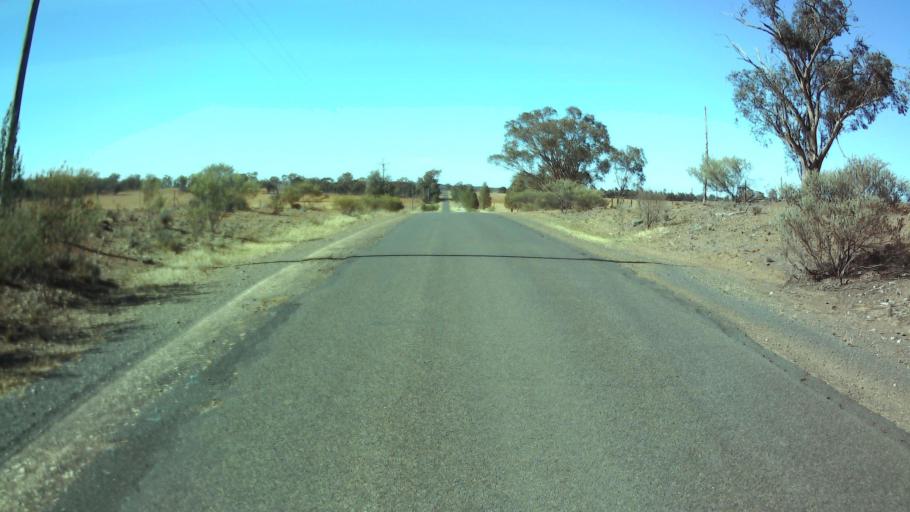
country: AU
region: New South Wales
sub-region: Weddin
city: Grenfell
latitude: -33.7631
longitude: 147.8291
